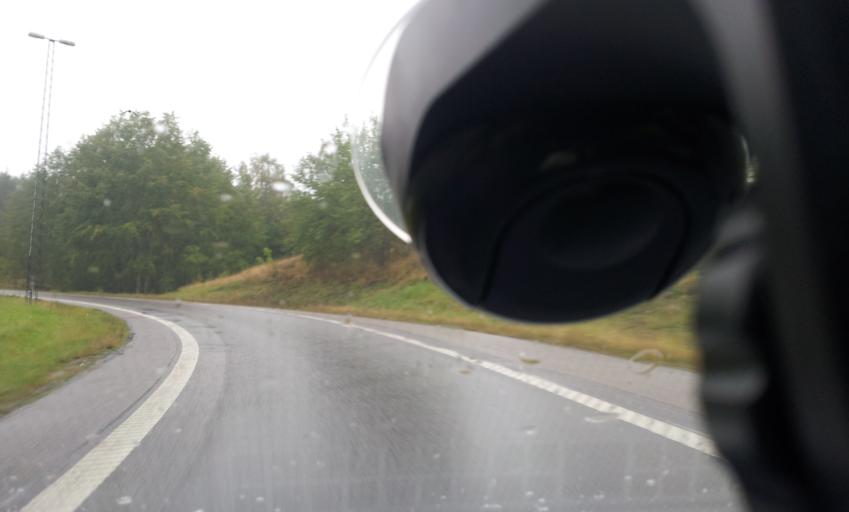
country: SE
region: OEstergoetland
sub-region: Norrkopings Kommun
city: Norrkoping
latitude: 58.5839
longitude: 16.1392
